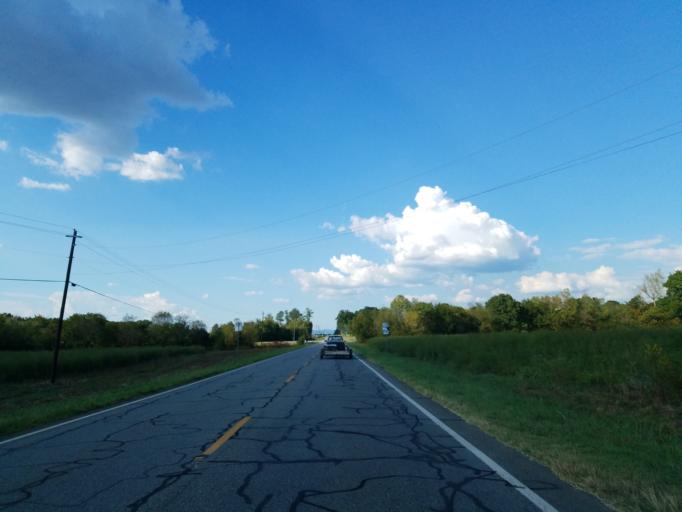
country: US
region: Georgia
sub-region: Bartow County
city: Rydal
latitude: 34.5266
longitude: -84.7066
